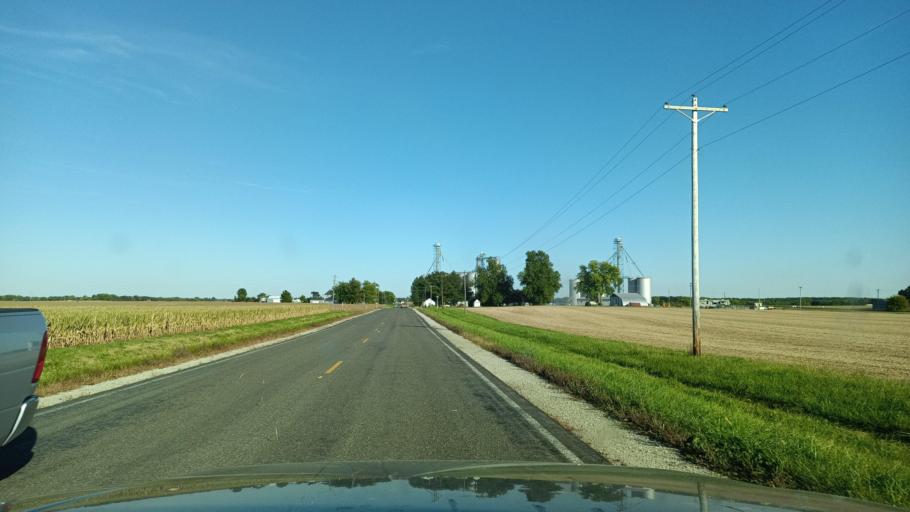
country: US
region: Illinois
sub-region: De Witt County
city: Farmer City
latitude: 40.2239
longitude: -88.7247
